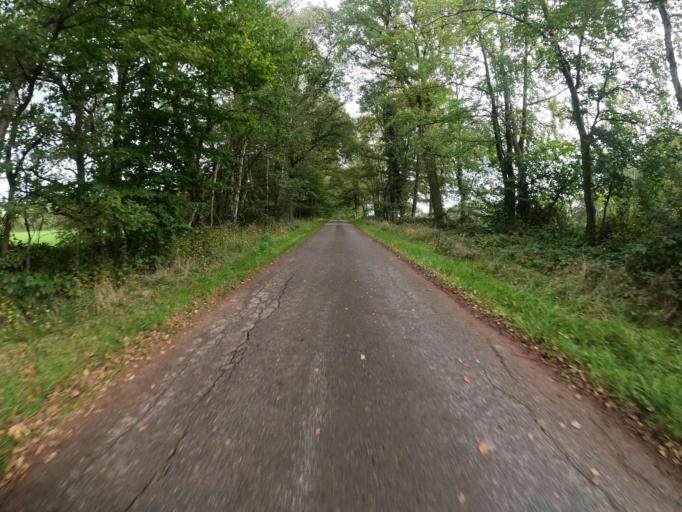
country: DE
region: North Rhine-Westphalia
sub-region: Regierungsbezirk Dusseldorf
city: Schermbeck
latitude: 51.7146
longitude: 6.8476
